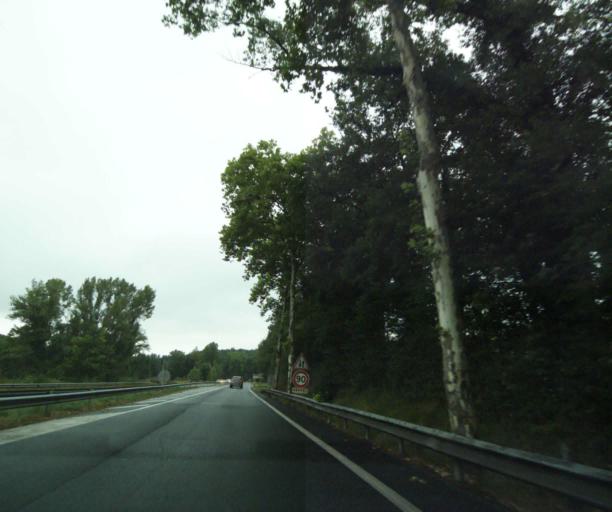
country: FR
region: Midi-Pyrenees
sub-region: Departement du Tarn
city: Le Garric
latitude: 43.9886
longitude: 2.1744
